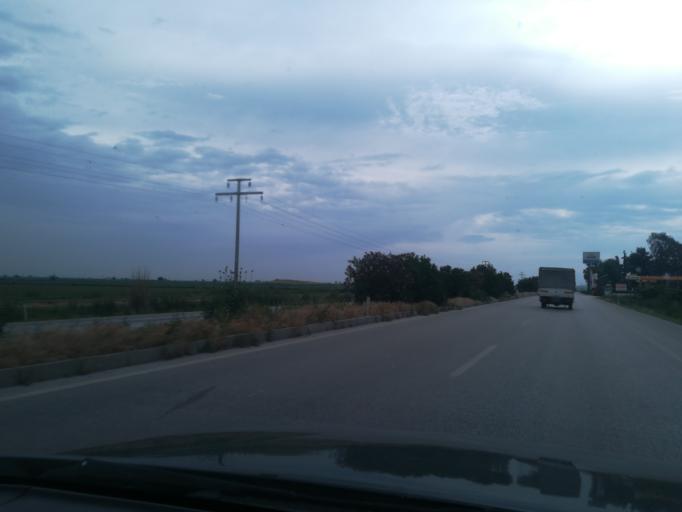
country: TR
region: Adana
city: Ceyhan
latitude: 37.0538
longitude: 35.8536
